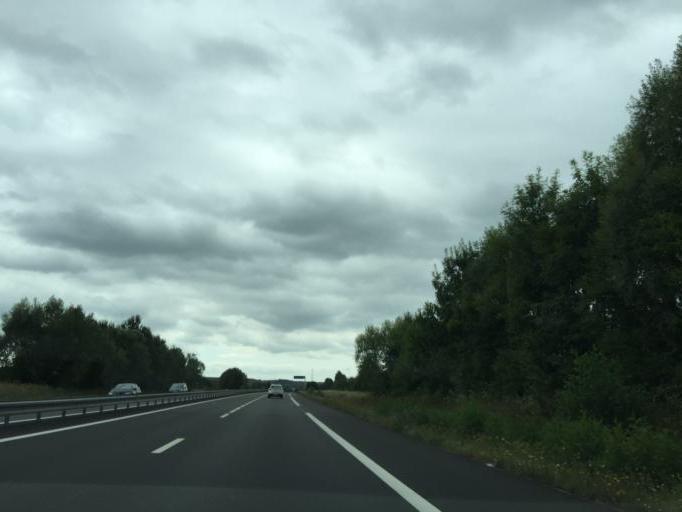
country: FR
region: Pays de la Loire
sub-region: Departement de la Sarthe
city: Teloche
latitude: 47.8883
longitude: 0.3051
